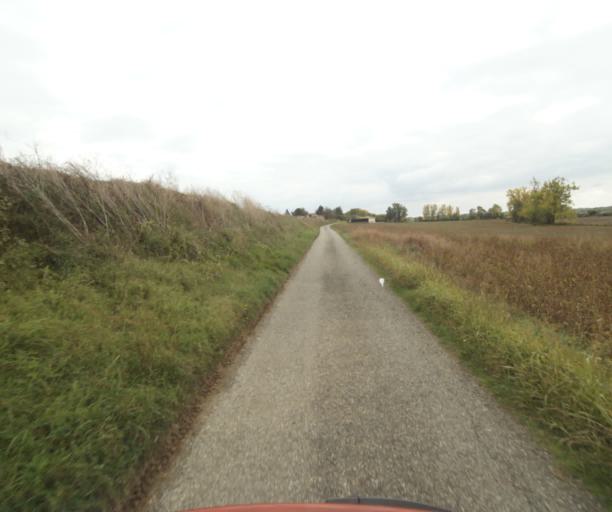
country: FR
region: Midi-Pyrenees
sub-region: Departement du Tarn-et-Garonne
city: Finhan
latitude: 43.8980
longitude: 1.2303
